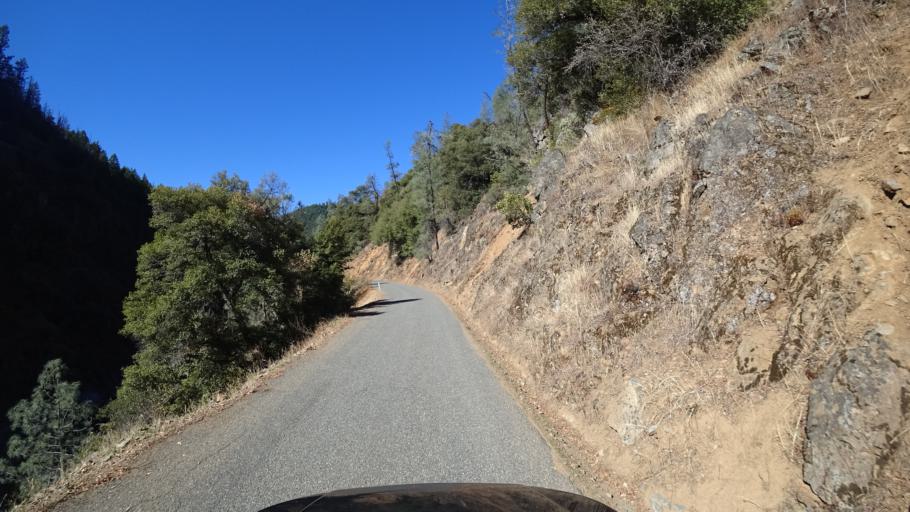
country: US
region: California
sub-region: Humboldt County
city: Willow Creek
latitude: 41.2203
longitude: -123.2424
